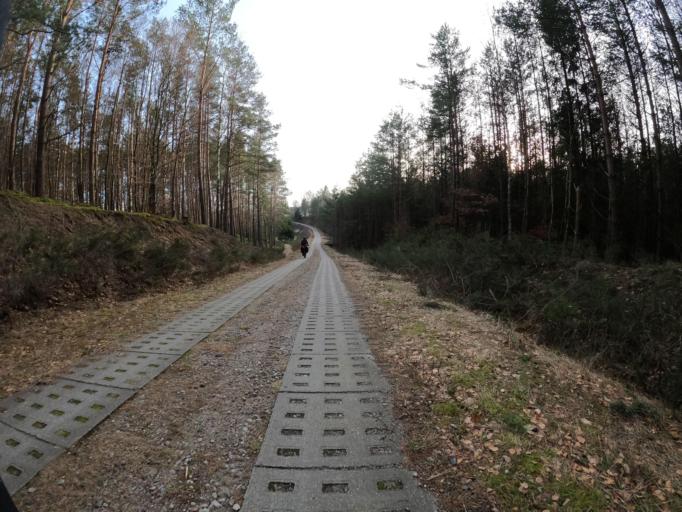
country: PL
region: West Pomeranian Voivodeship
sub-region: Powiat koszalinski
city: Polanow
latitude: 54.1282
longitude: 16.6638
